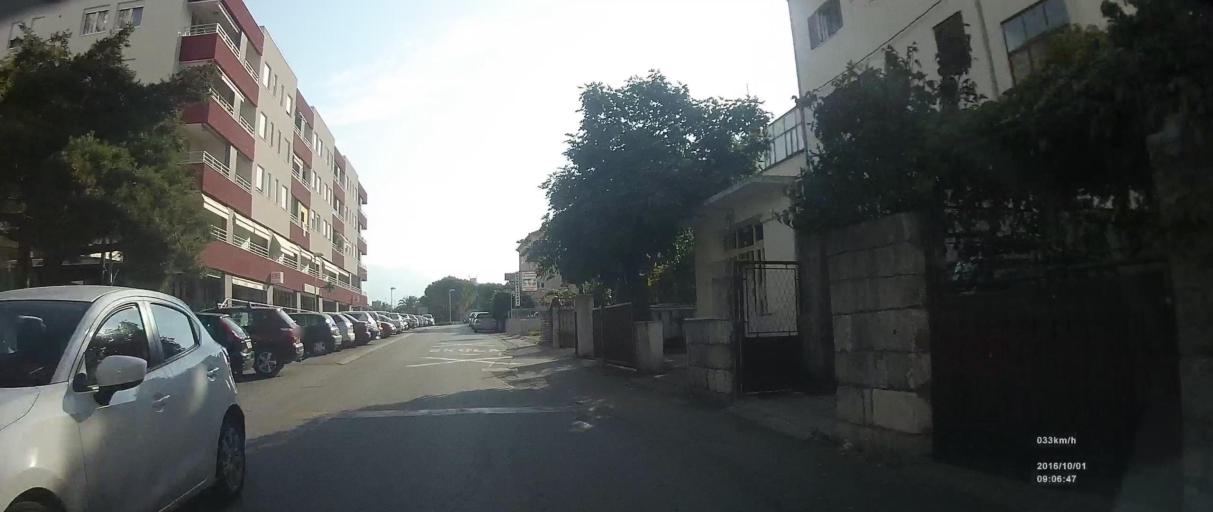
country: HR
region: Splitsko-Dalmatinska
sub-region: Grad Split
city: Split
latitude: 43.5192
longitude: 16.4528
